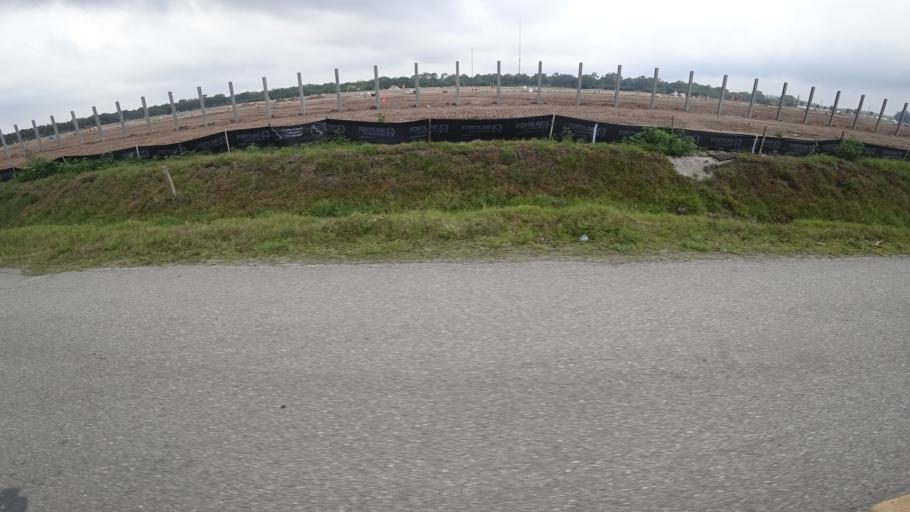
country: US
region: Florida
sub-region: Manatee County
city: Samoset
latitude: 27.4736
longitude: -82.5137
